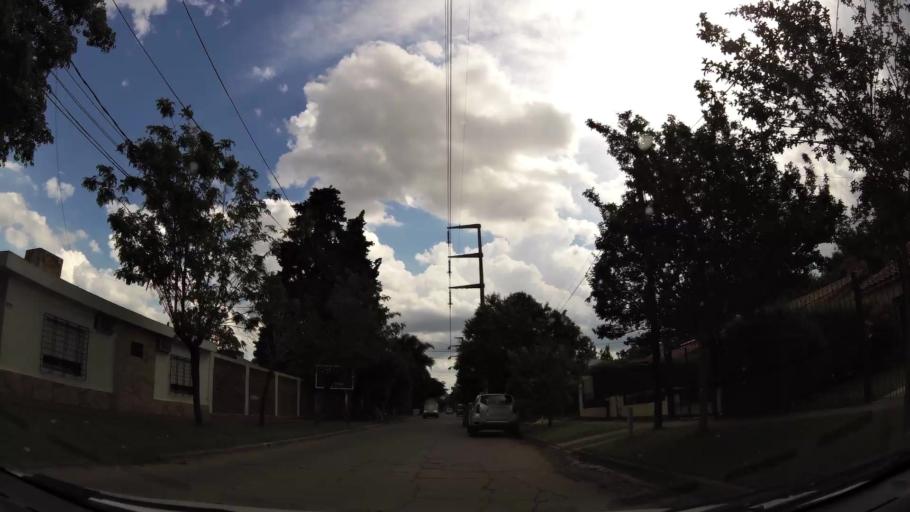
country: AR
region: Buenos Aires
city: Ituzaingo
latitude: -34.6351
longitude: -58.6802
